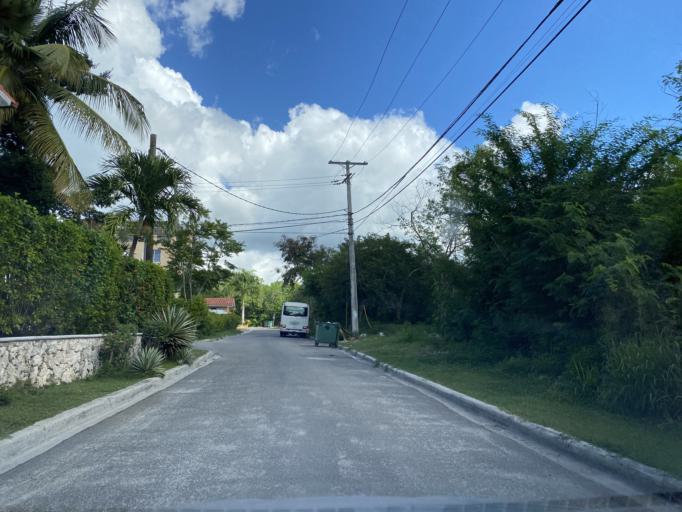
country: DO
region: La Romana
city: La Romana
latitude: 18.3474
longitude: -68.8252
